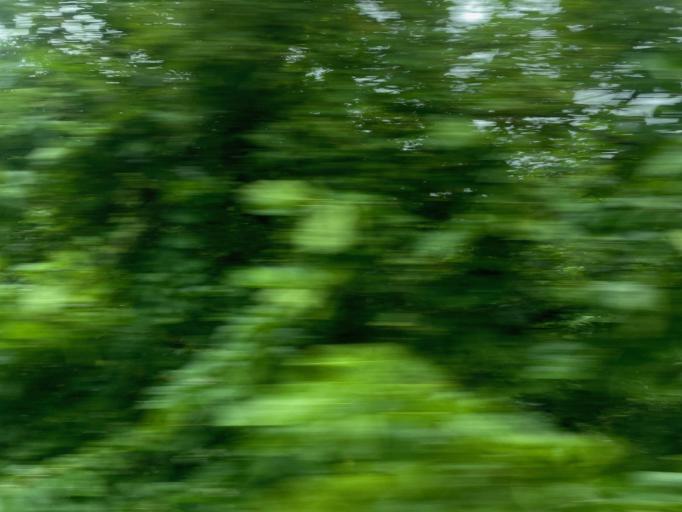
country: JP
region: Fukushima
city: Fukushima-shi
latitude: 37.6615
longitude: 140.4805
